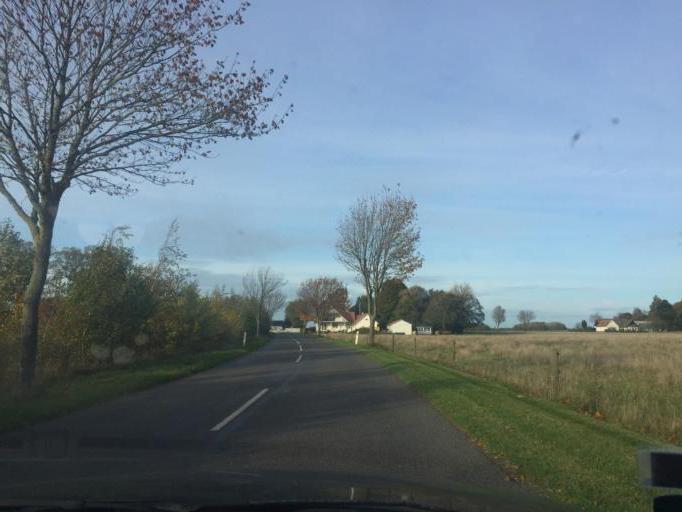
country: DK
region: Zealand
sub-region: Stevns Kommune
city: Store Heddinge
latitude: 55.2713
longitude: 12.4166
